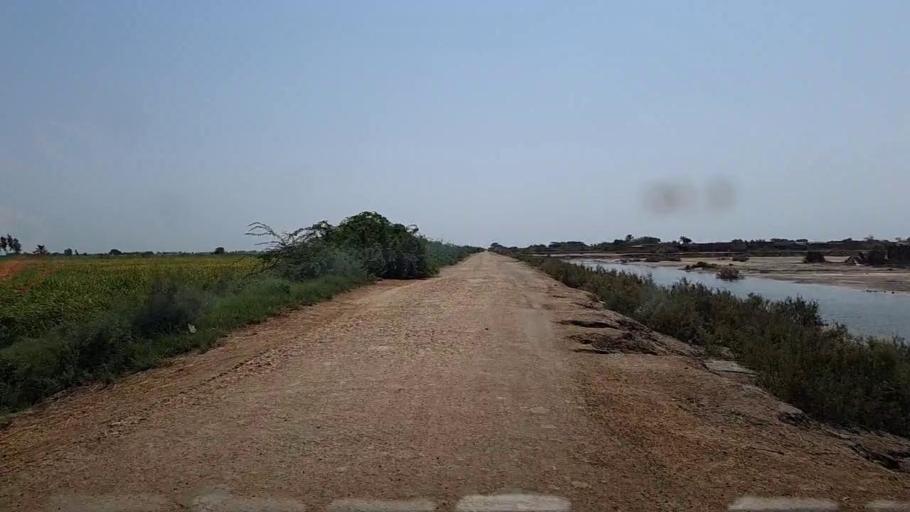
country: PK
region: Sindh
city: Mirpur Batoro
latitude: 24.6330
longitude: 68.4522
